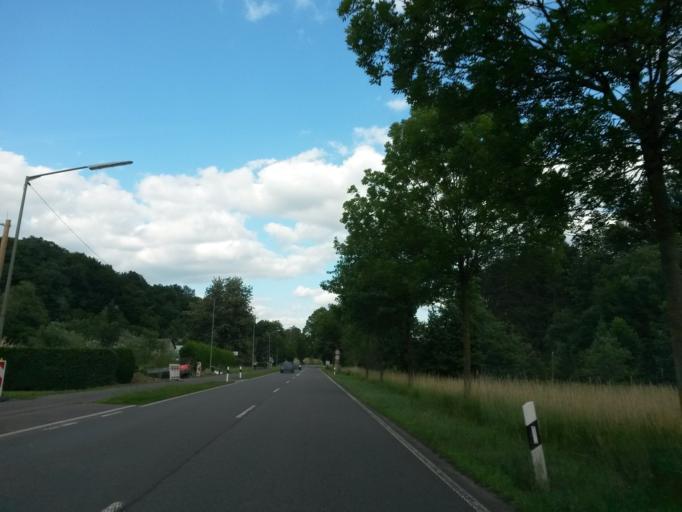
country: DE
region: North Rhine-Westphalia
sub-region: Regierungsbezirk Koln
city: Numbrecht
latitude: 50.8598
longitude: 7.5398
